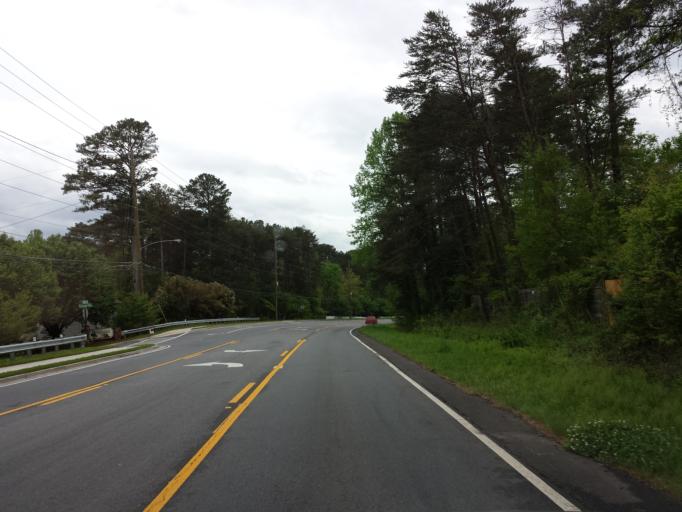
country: US
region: Georgia
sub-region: Cherokee County
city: Woodstock
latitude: 34.0722
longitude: -84.4903
